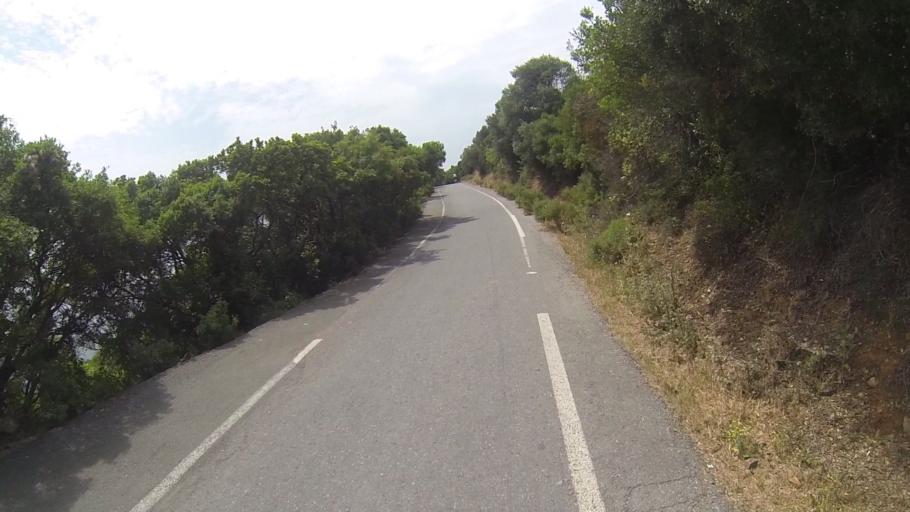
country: TR
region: Istanbul
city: Adalar
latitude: 40.8394
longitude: 29.1174
